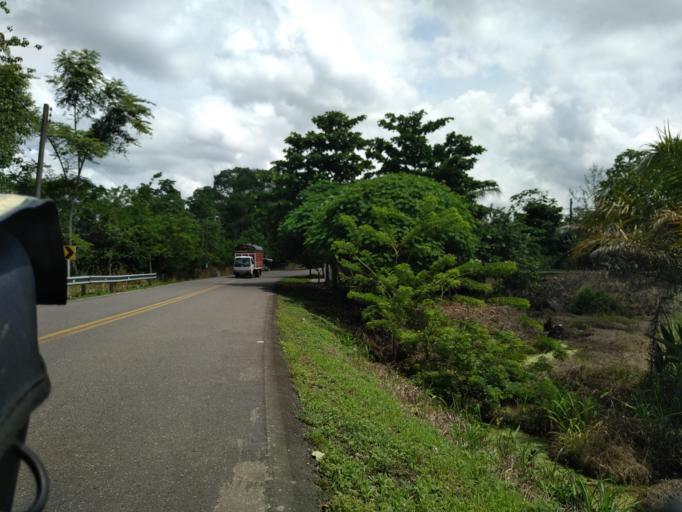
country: CO
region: Santander
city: Puerto Parra
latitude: 6.5225
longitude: -74.0833
